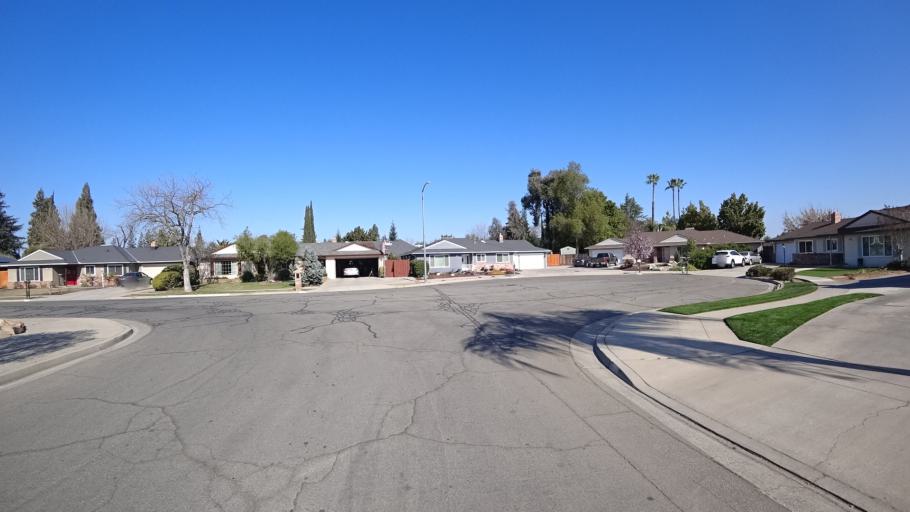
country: US
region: California
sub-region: Fresno County
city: Fresno
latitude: 36.8461
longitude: -119.8138
